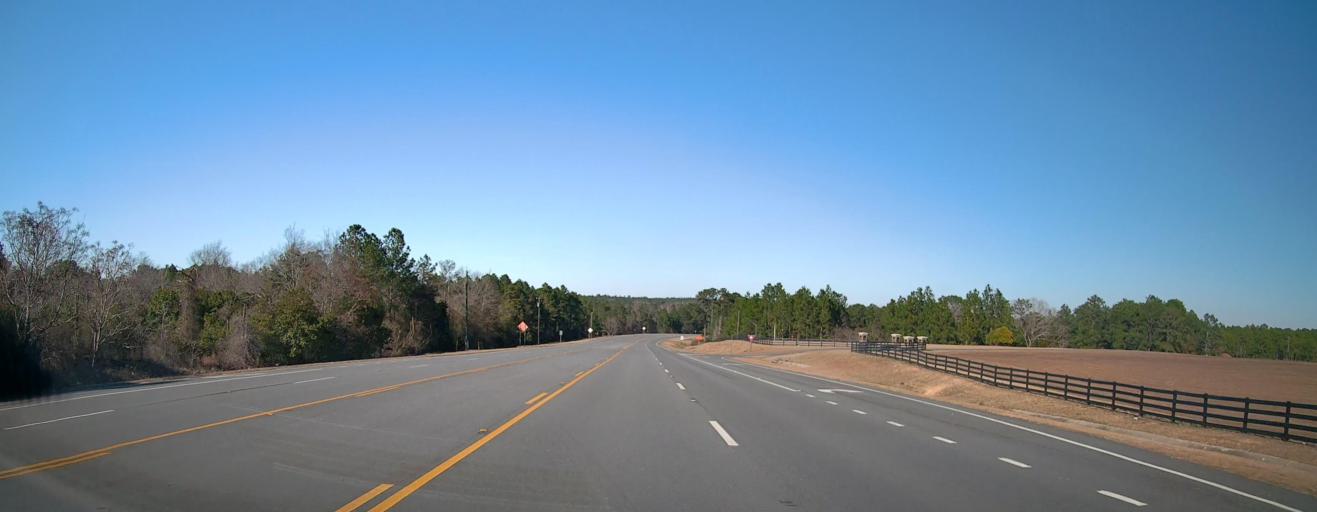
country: US
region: Georgia
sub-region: Taylor County
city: Butler
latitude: 32.5782
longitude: -84.2385
